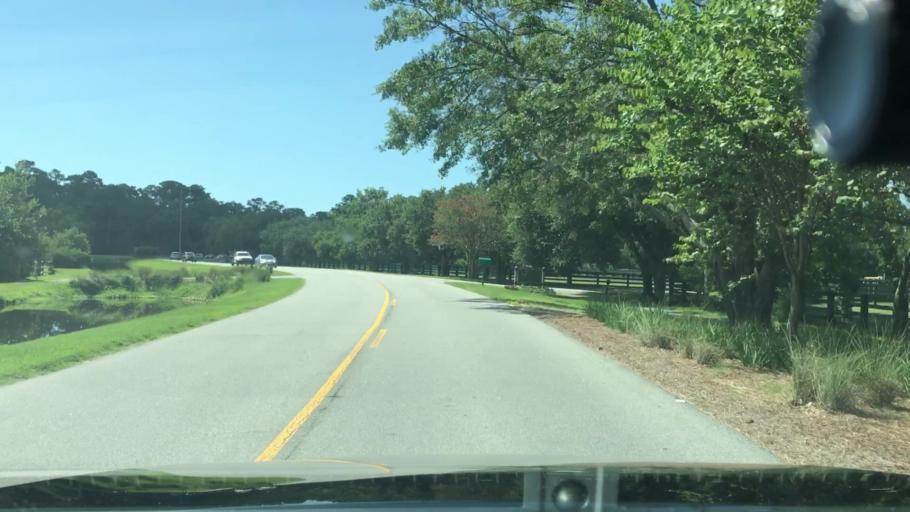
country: US
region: South Carolina
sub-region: Beaufort County
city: Hilton Head Island
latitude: 32.1424
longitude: -80.7893
